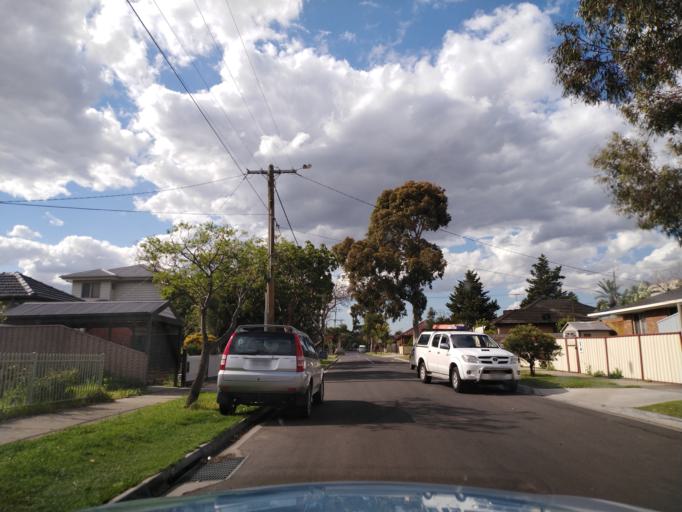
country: AU
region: Victoria
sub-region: Hobsons Bay
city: South Kingsville
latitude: -37.8451
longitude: 144.8650
